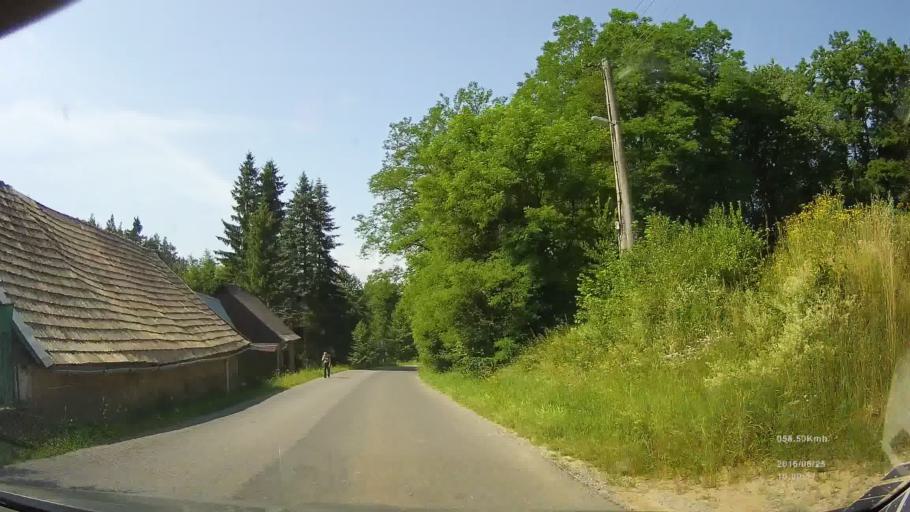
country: SK
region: Banskobystricky
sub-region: Okres Banska Bystrica
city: Zvolen
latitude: 48.6391
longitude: 19.2076
